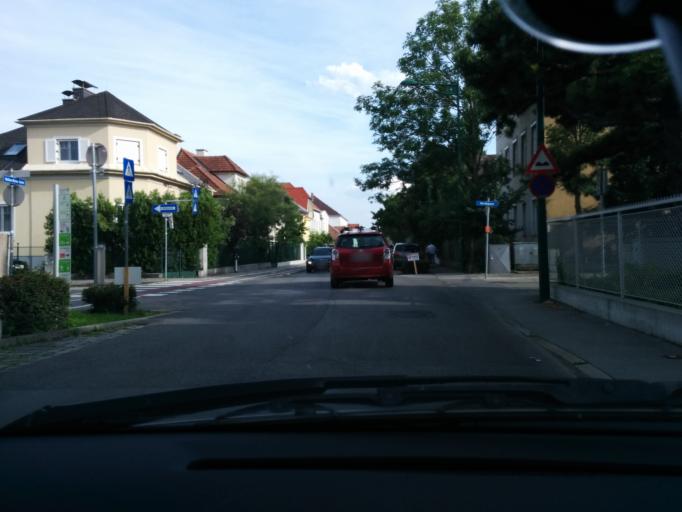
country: AT
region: Lower Austria
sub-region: Politischer Bezirk Modling
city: Modling
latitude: 48.0815
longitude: 16.2943
